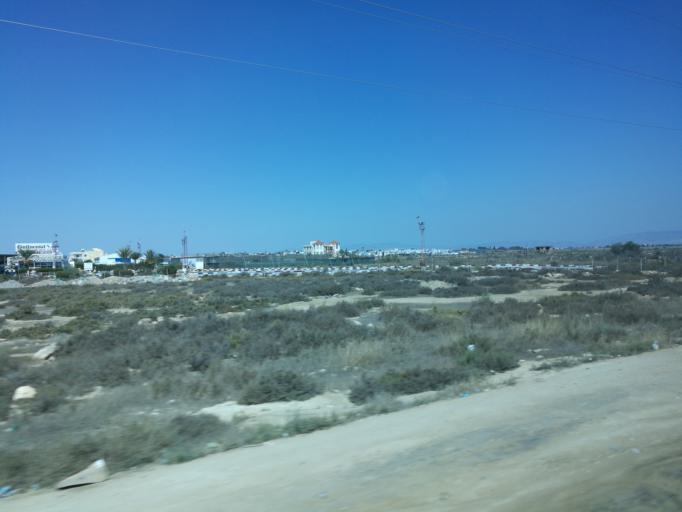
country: CY
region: Ammochostos
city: Famagusta
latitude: 35.1603
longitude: 33.8997
